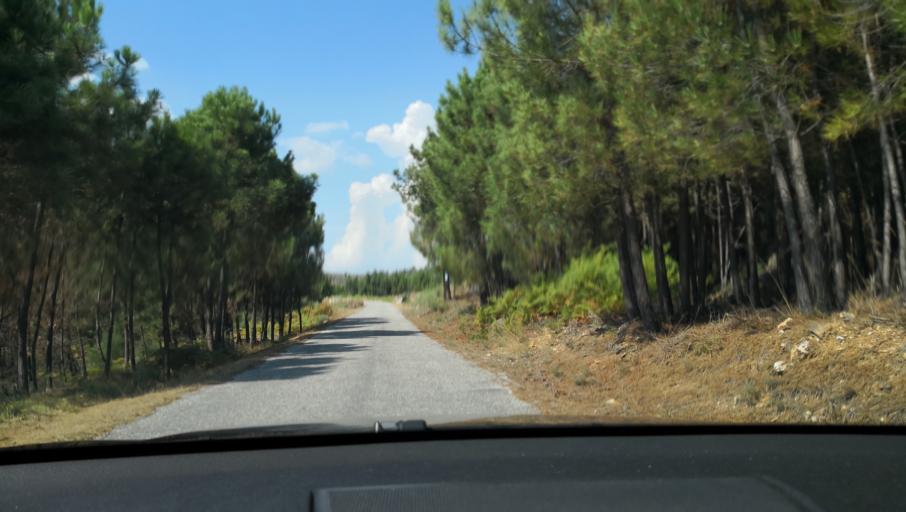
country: PT
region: Vila Real
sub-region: Sabrosa
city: Sabrosa
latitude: 41.3056
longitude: -7.5826
